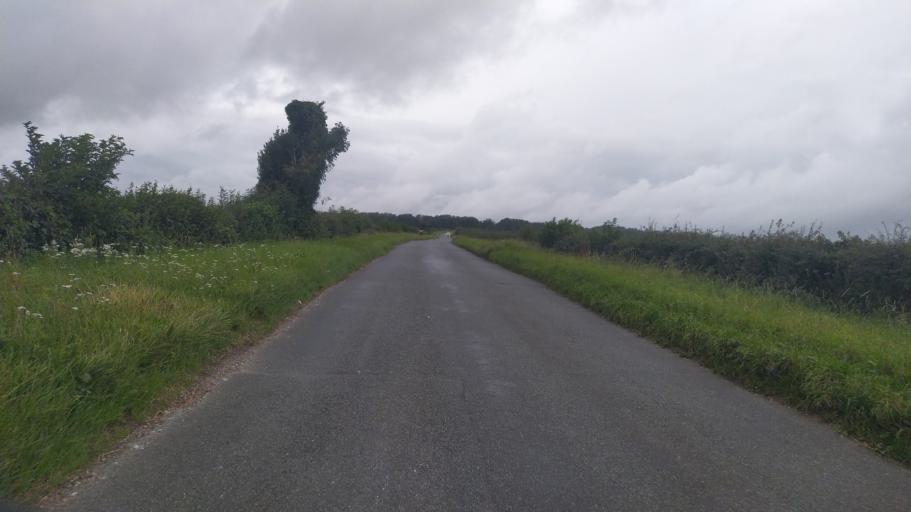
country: GB
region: England
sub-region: Dorset
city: Dorchester
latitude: 50.7984
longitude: -2.4413
